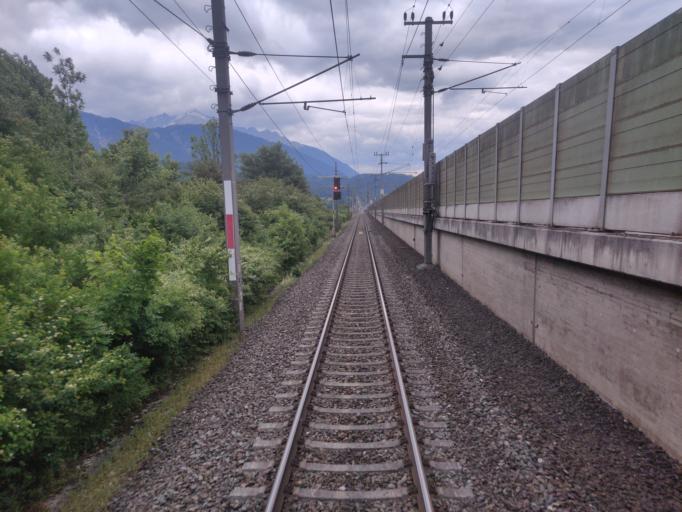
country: AT
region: Tyrol
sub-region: Politischer Bezirk Innsbruck Land
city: Volders
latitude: 47.2858
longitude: 11.5468
